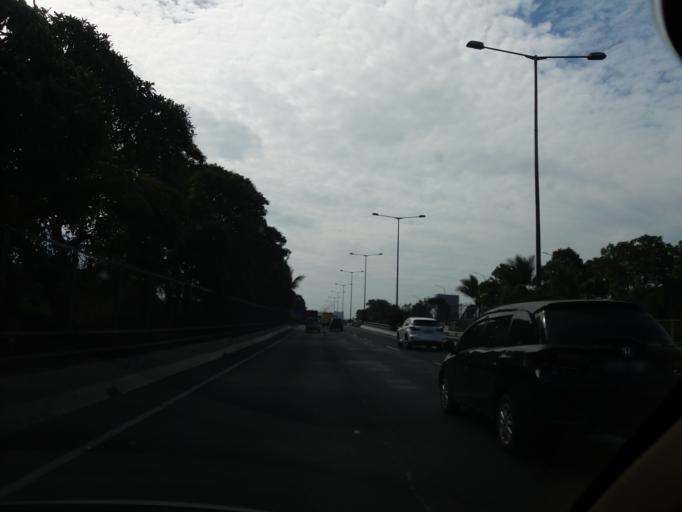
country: ID
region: Jakarta Raya
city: Jakarta
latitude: -6.2162
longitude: 106.8741
